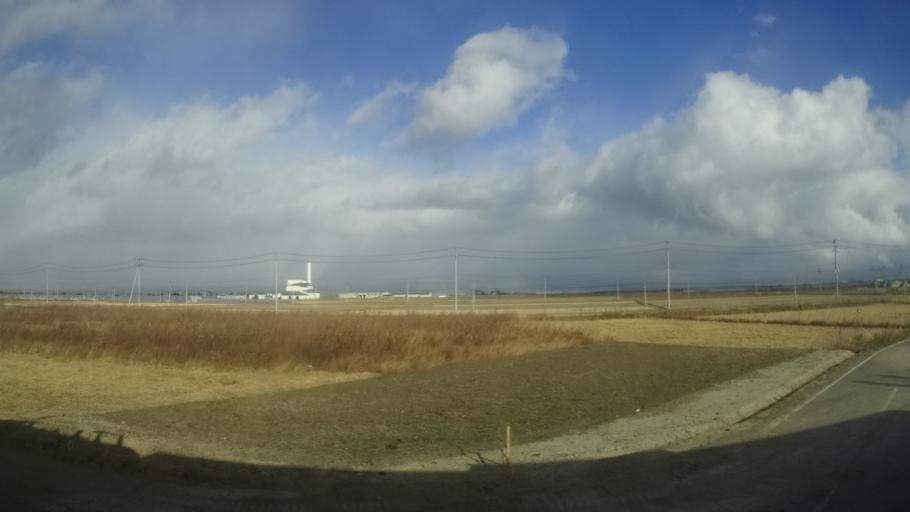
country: JP
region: Miyagi
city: Watari
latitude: 37.9513
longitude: 140.8959
